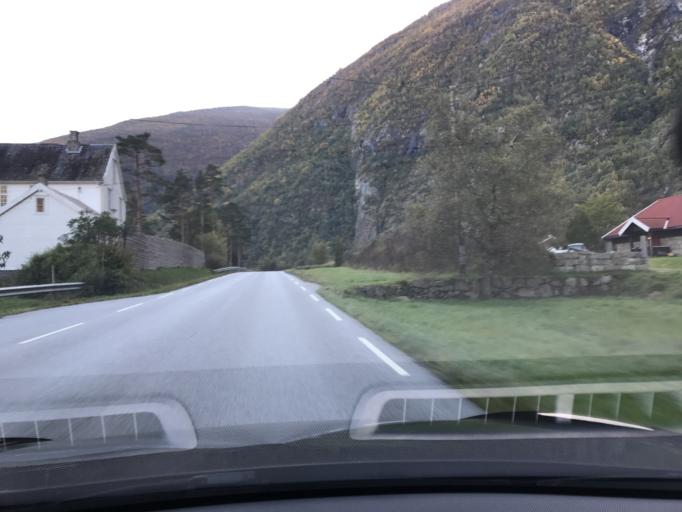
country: NO
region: Sogn og Fjordane
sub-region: Laerdal
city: Laerdalsoyri
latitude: 61.0754
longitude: 7.5014
